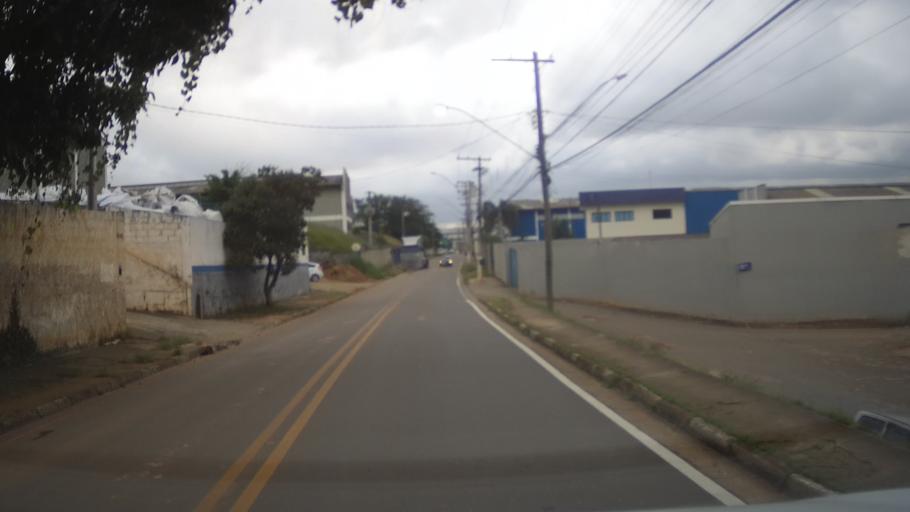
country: BR
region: Sao Paulo
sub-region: Aruja
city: Aruja
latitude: -23.4055
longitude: -46.3585
